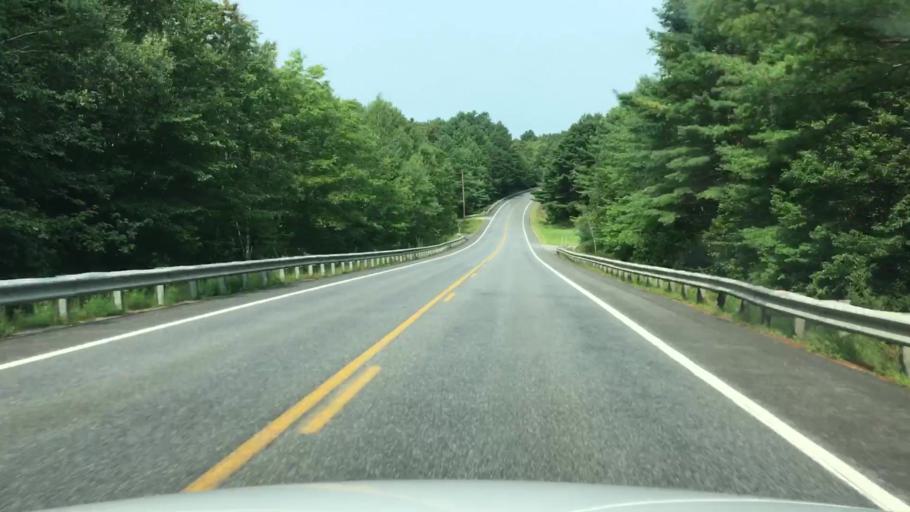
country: US
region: Maine
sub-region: Kennebec County
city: Winthrop
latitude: 44.3330
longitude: -70.0081
